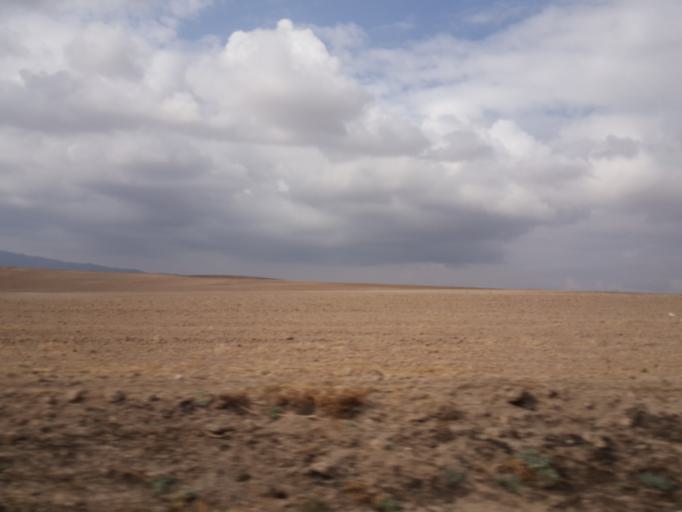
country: TR
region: Kirikkale
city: Keskin
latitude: 39.6130
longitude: 33.6131
